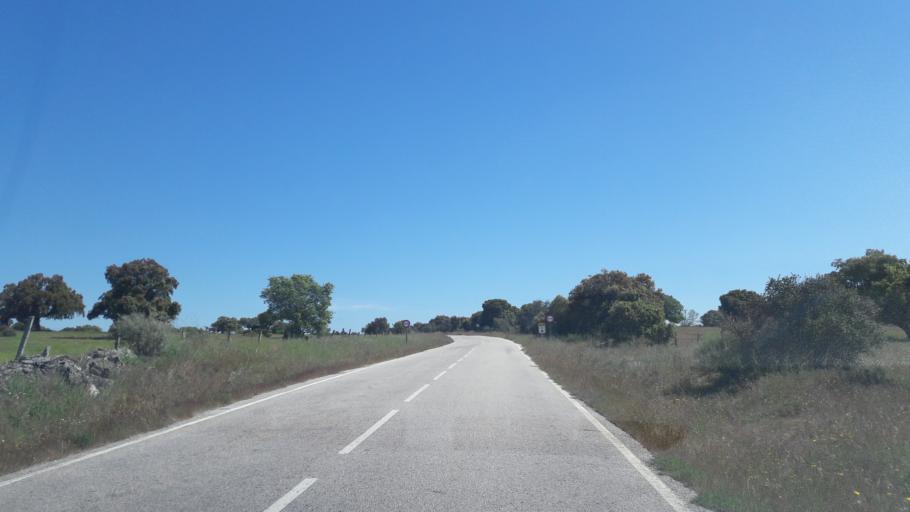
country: ES
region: Castille and Leon
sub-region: Provincia de Salamanca
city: Villarmuerto
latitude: 41.0363
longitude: -6.3947
